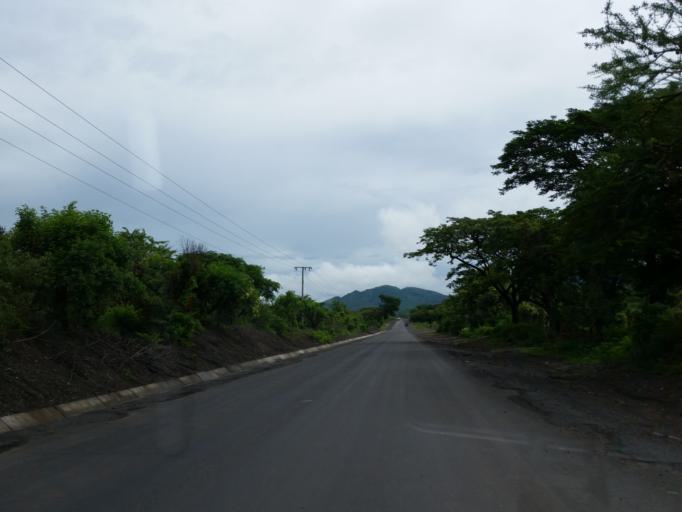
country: NI
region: Leon
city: La Paz Centro
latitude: 12.4218
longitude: -86.6421
